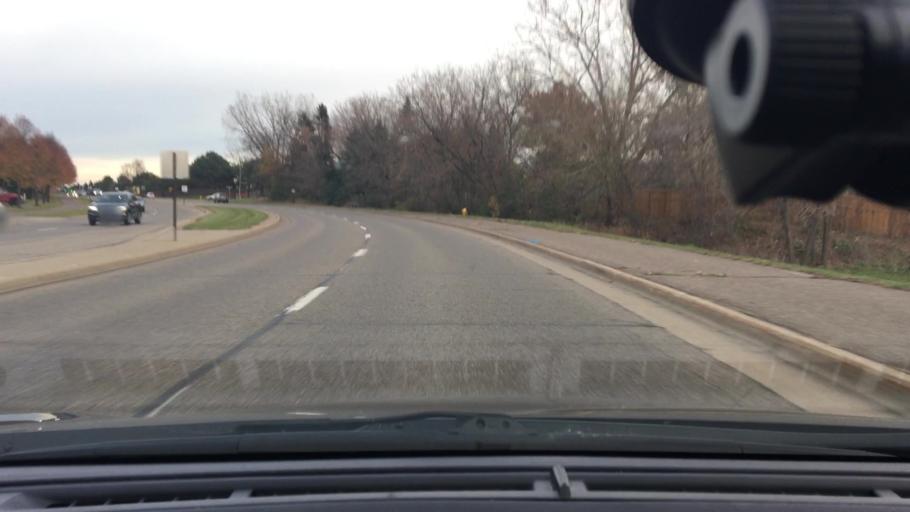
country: US
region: Minnesota
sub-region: Hennepin County
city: Maple Grove
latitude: 45.0586
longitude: -93.4282
